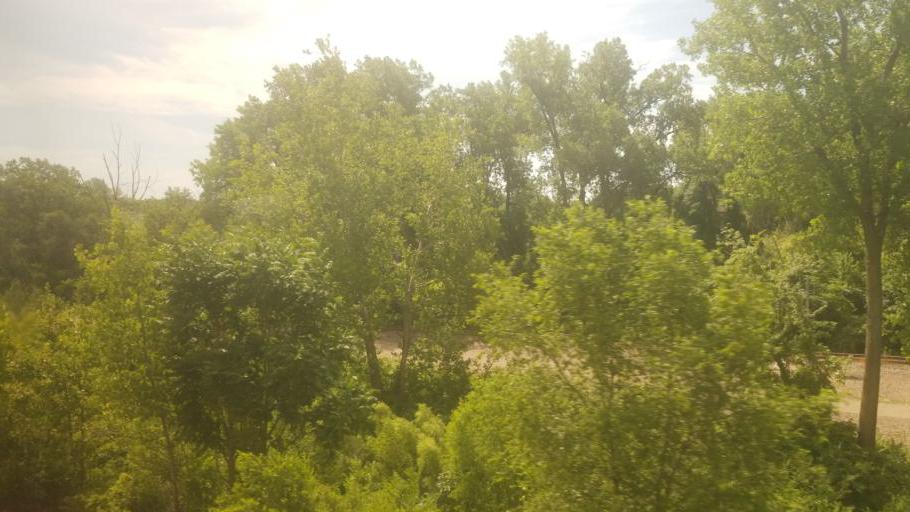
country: US
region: Missouri
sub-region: Jackson County
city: Sugar Creek
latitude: 39.1136
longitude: -94.4771
